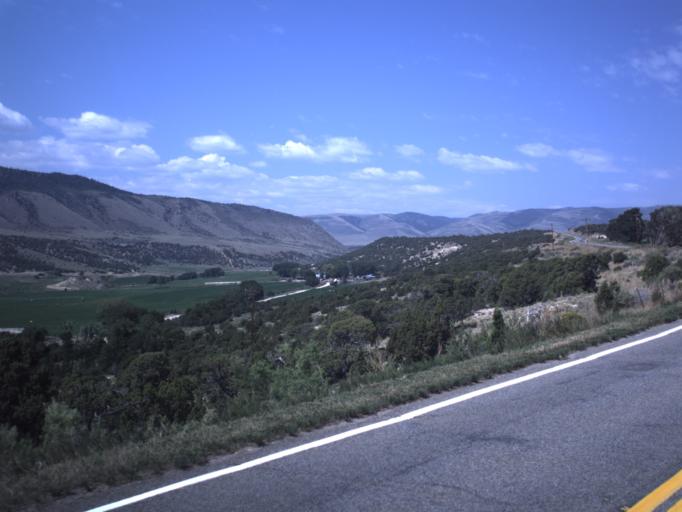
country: US
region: Utah
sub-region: Daggett County
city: Manila
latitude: 40.9788
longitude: -109.7862
